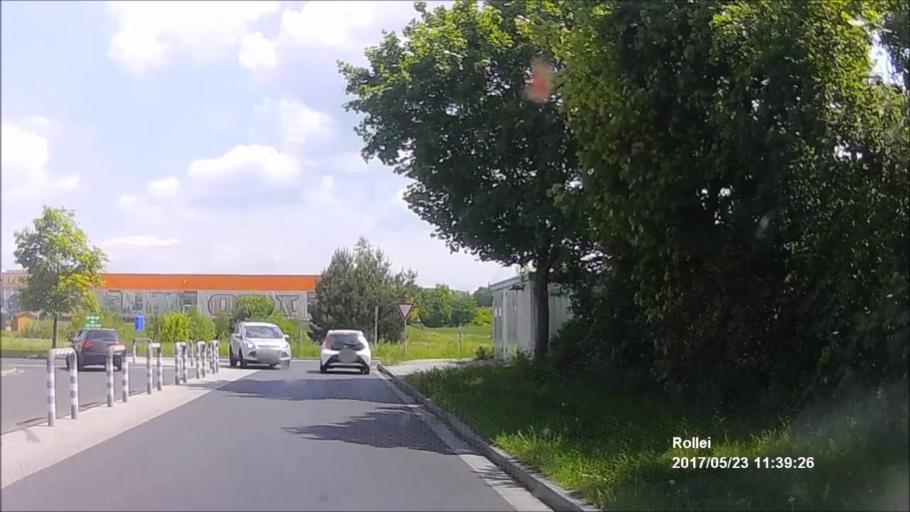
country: DE
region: Bavaria
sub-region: Upper Palatinate
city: Wackersdorf
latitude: 49.3125
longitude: 12.1477
